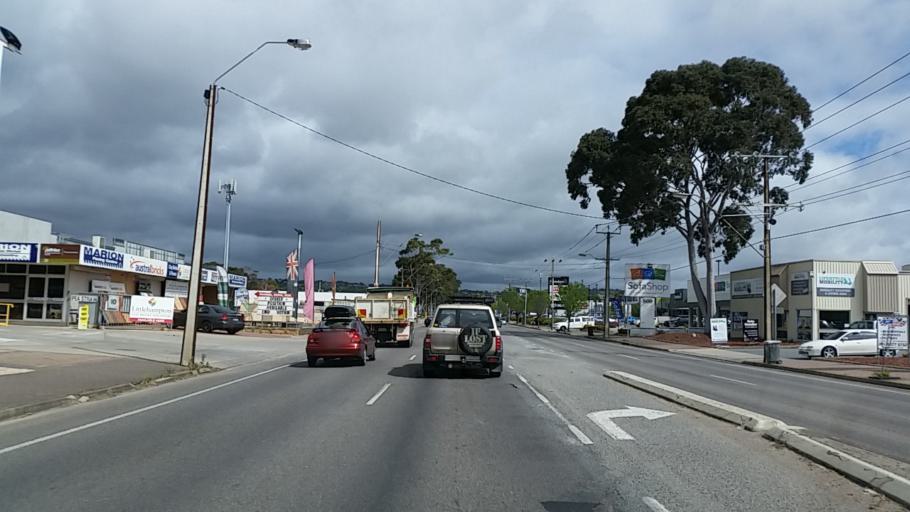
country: AU
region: South Australia
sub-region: Marion
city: Sturt
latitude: -35.0091
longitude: 138.5582
